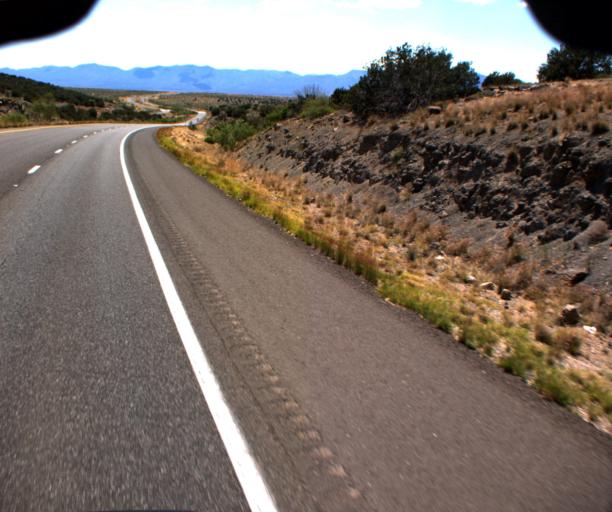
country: US
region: Arizona
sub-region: Yavapai County
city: Cornville
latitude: 34.7904
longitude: -111.9185
